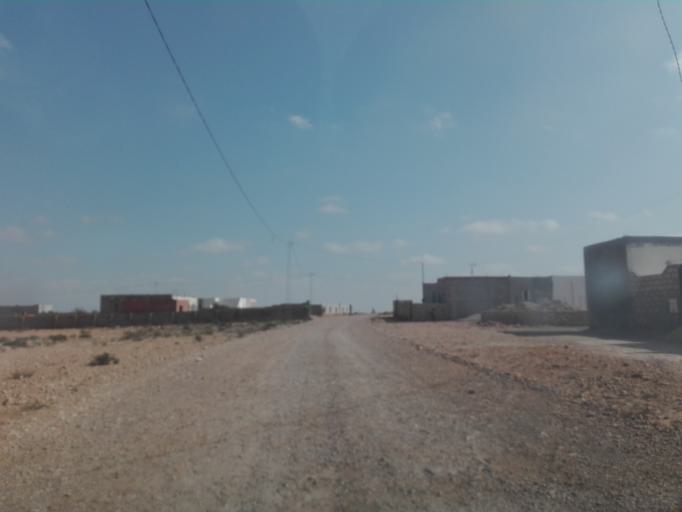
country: TN
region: Madanin
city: Medenine
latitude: 33.4306
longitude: 10.4079
